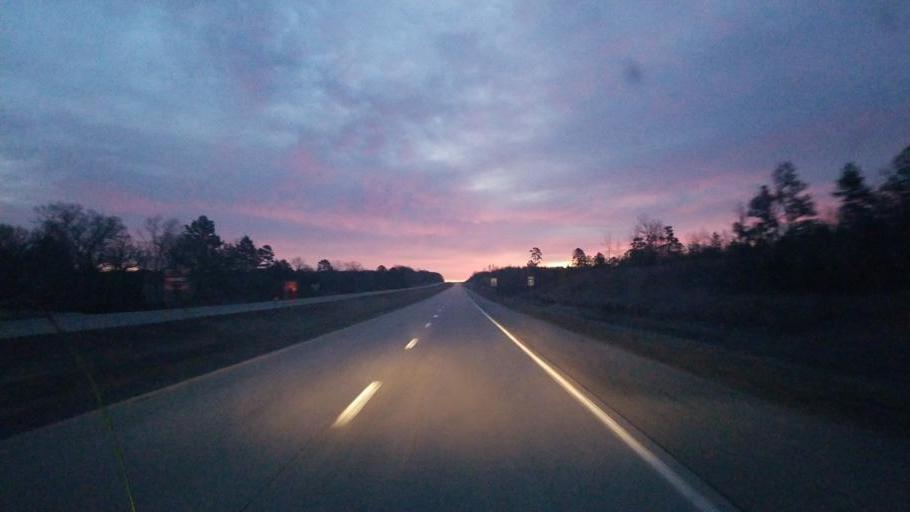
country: US
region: Missouri
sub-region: Shannon County
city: Winona
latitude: 36.9990
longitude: -91.4221
